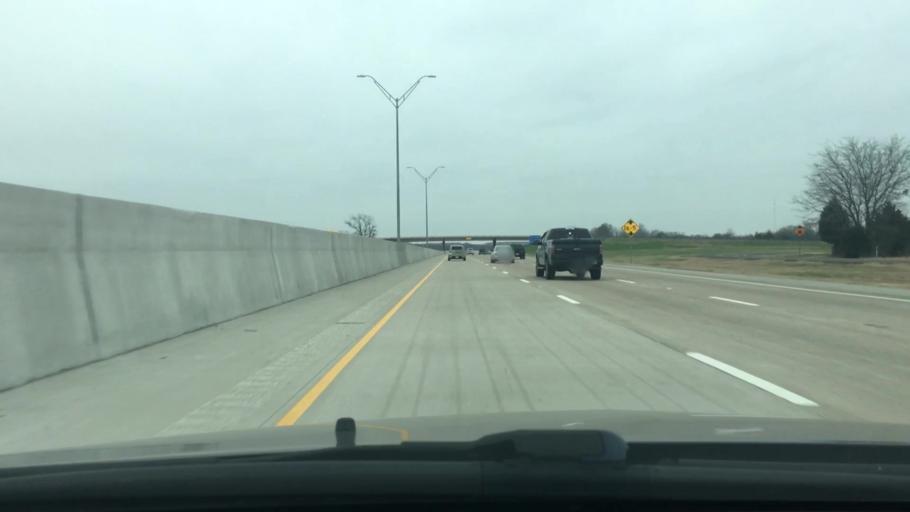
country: US
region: Texas
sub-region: Freestone County
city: Wortham
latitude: 31.9294
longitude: -96.4209
